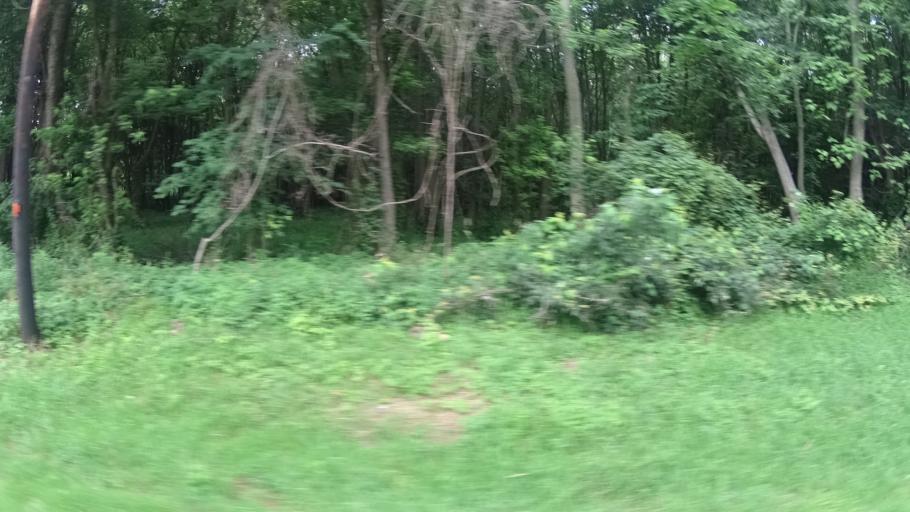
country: US
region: Ohio
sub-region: Huron County
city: Wakeman
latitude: 41.3070
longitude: -82.4812
